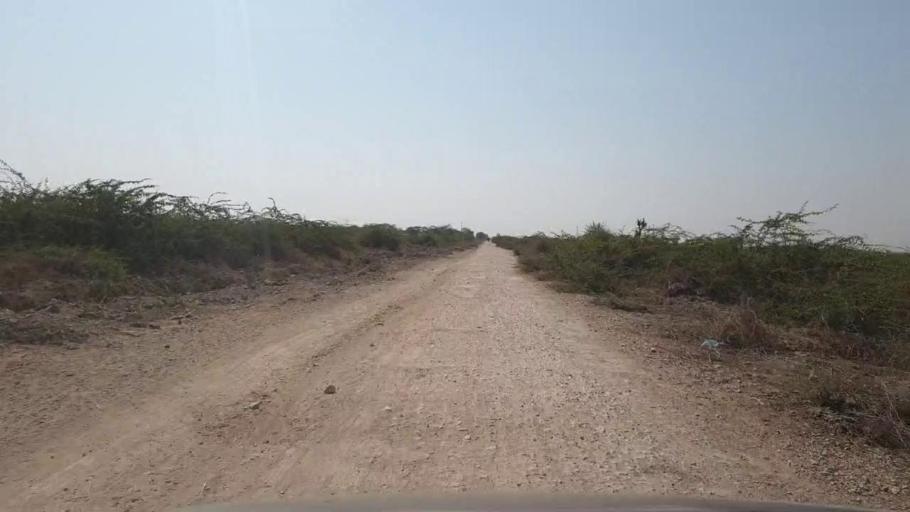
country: PK
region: Sindh
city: Digri
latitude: 25.2037
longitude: 69.2296
